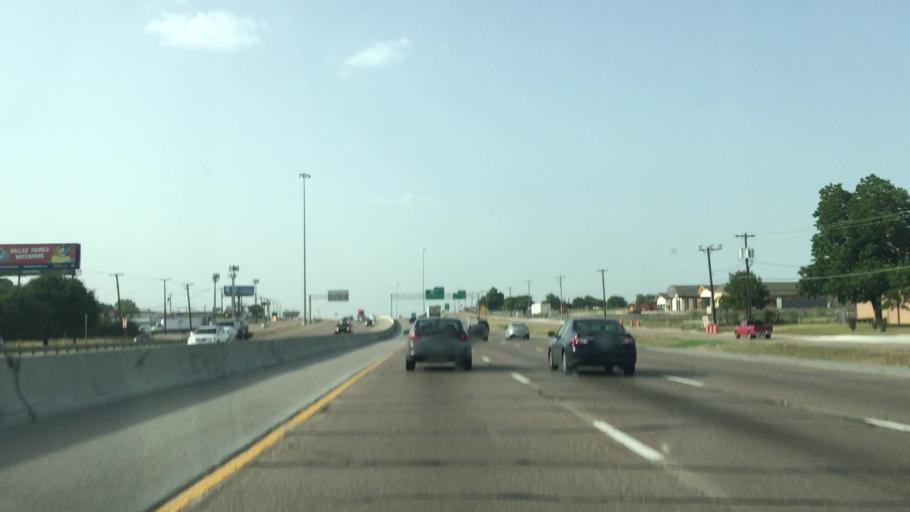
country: US
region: Texas
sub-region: Dallas County
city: DeSoto
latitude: 32.6686
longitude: -96.8227
